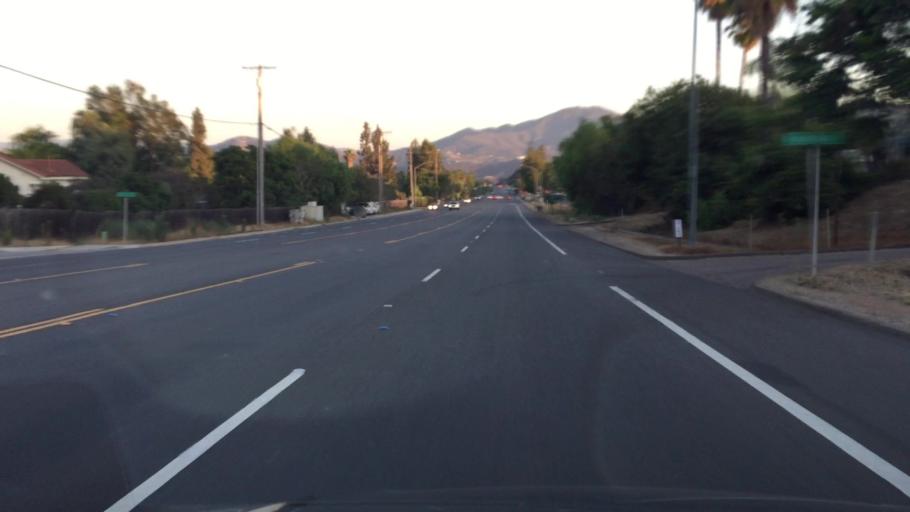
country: US
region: California
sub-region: San Diego County
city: Rancho San Diego
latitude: 32.7732
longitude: -116.9280
